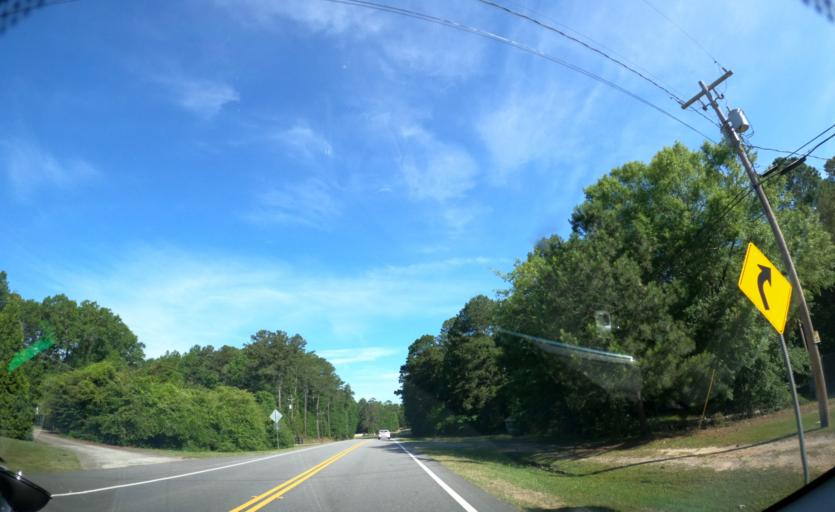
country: US
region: Georgia
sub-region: Columbia County
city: Appling
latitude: 33.6594
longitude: -82.3323
